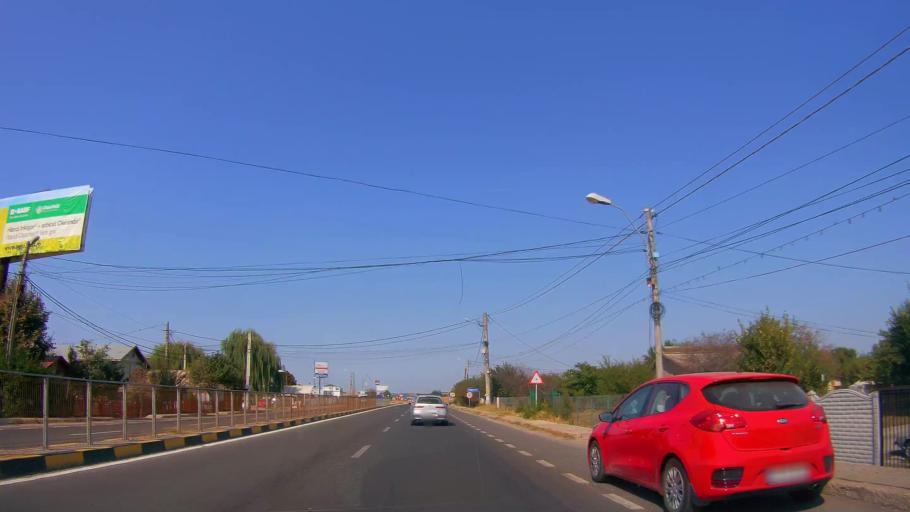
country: RO
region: Giurgiu
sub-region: Comuna Fratesti
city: Remus
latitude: 43.9480
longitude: 25.9802
